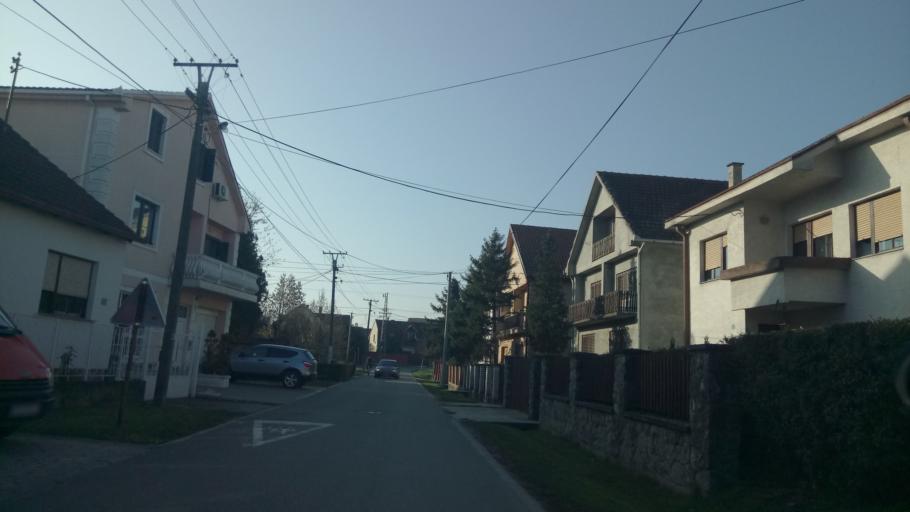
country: RS
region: Autonomna Pokrajina Vojvodina
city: Nova Pazova
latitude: 44.9430
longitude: 20.2149
